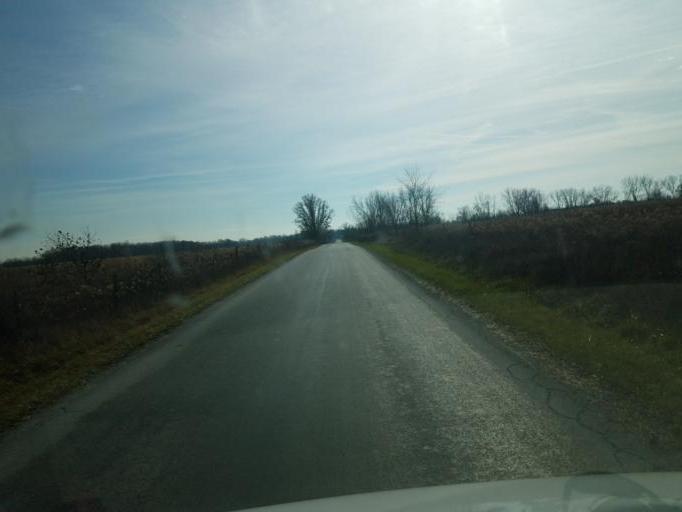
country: US
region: Ohio
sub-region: Hardin County
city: Kenton
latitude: 40.6210
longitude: -83.4386
